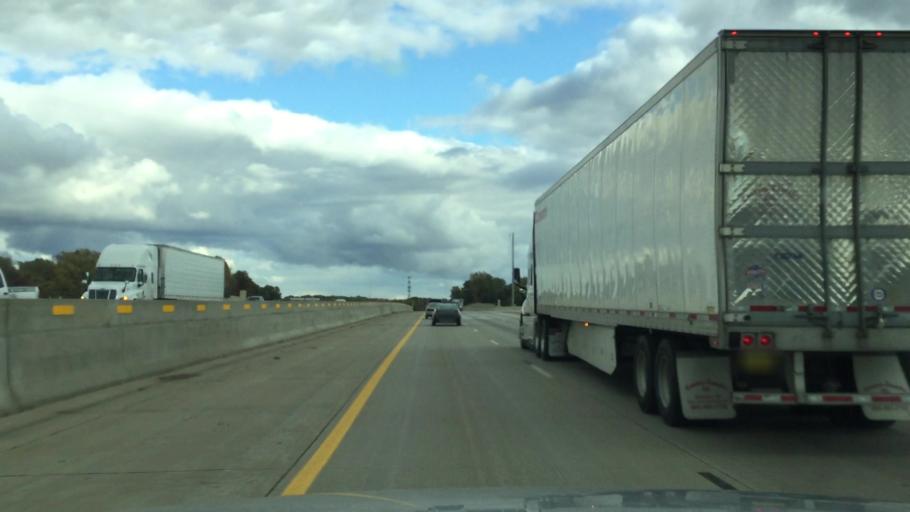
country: US
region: Michigan
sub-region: Kalamazoo County
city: Portage
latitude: 42.2370
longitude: -85.5915
